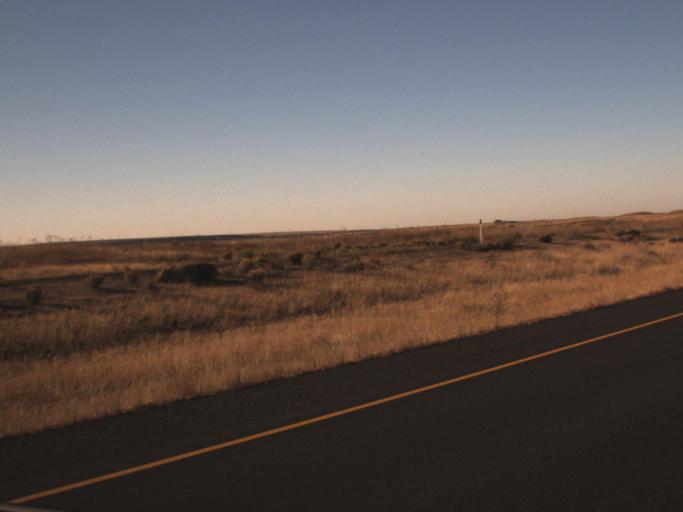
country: US
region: Washington
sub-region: Franklin County
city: Connell
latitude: 46.6101
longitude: -118.9144
